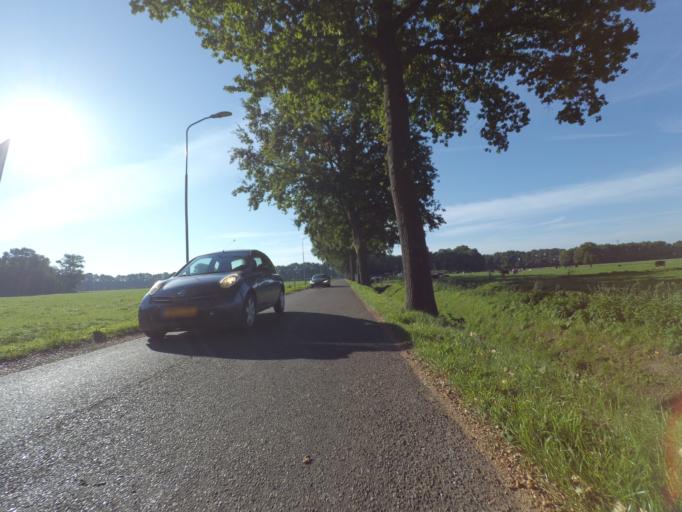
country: NL
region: Gelderland
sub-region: Gemeente Putten
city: Putten
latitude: 52.2652
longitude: 5.5788
